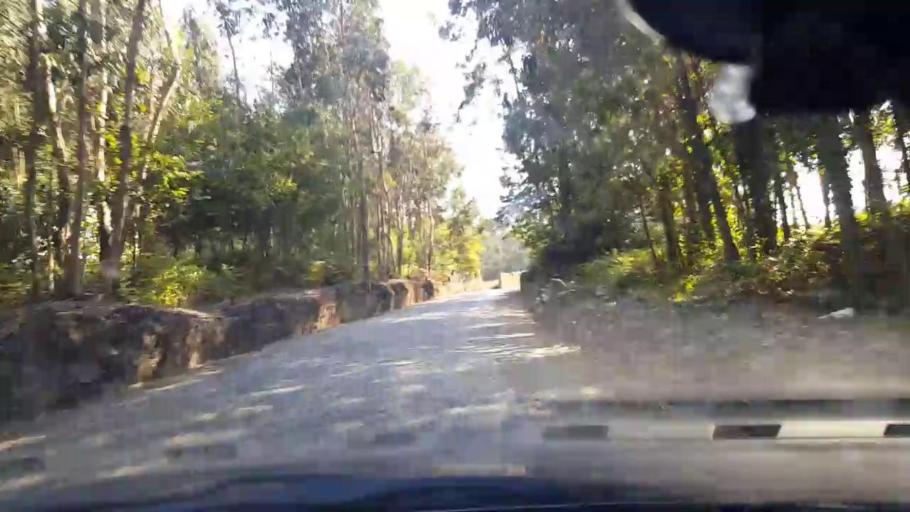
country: PT
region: Porto
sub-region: Vila do Conde
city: Arvore
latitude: 41.3561
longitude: -8.7022
